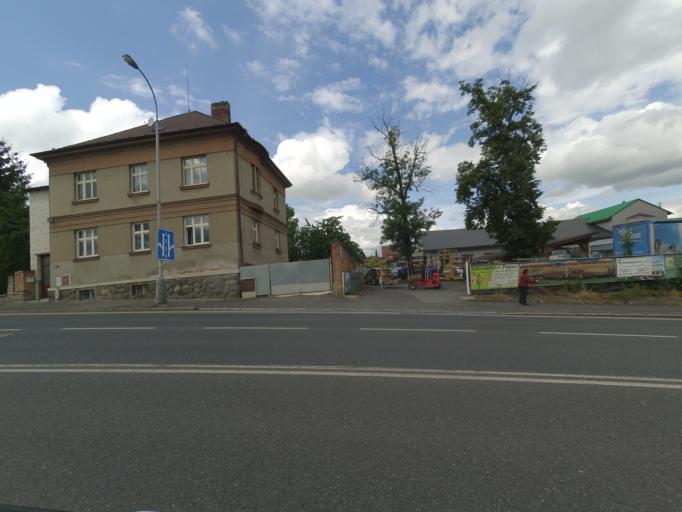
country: CZ
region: Plzensky
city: Klatovy
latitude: 49.3941
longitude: 13.2829
